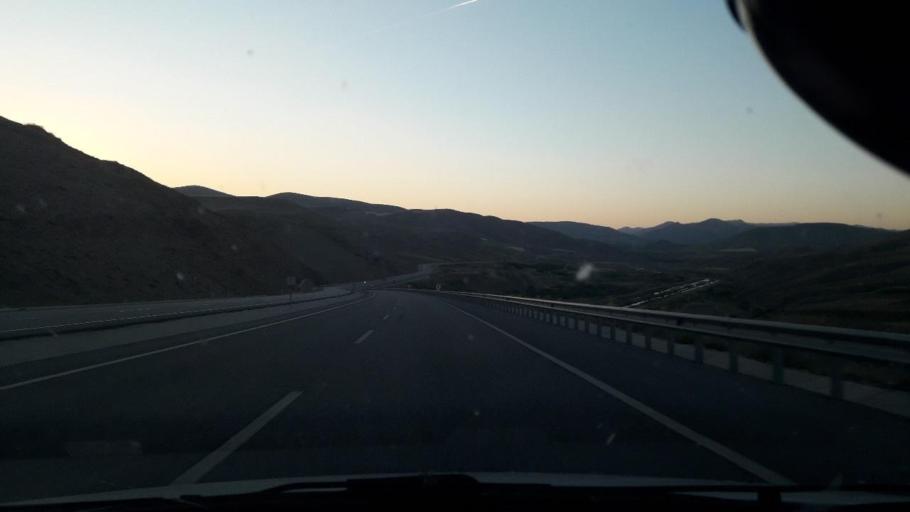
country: TR
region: Malatya
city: Yazihan
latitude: 38.6206
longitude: 38.1693
